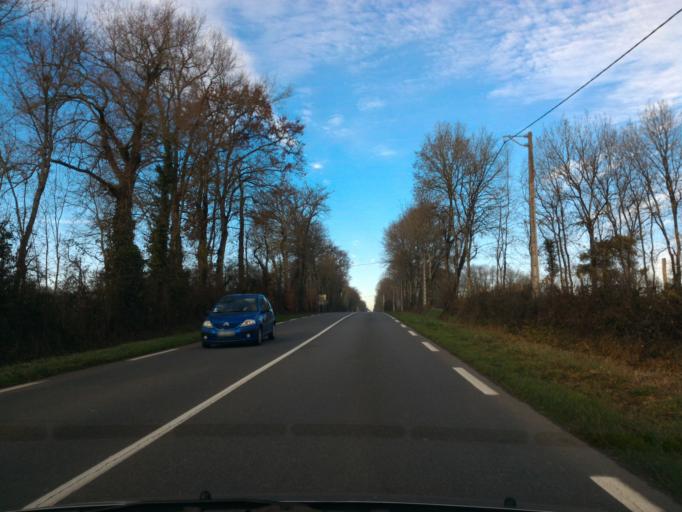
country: FR
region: Poitou-Charentes
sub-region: Departement de la Charente
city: Confolens
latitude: 46.0253
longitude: 0.6513
